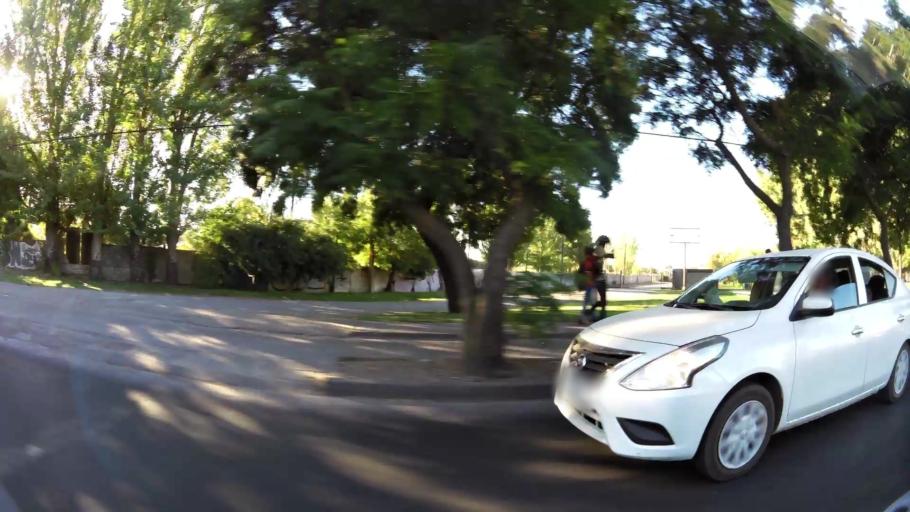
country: CL
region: Maule
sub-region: Provincia de Curico
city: Curico
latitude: -34.9755
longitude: -71.2289
